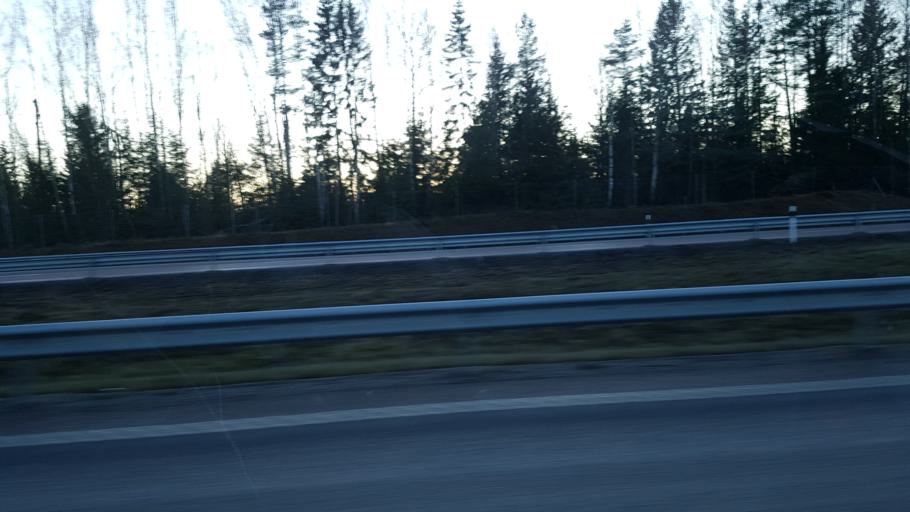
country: SE
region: Stockholm
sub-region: Nykvarns Kommun
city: Nykvarn
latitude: 59.2074
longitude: 17.3410
